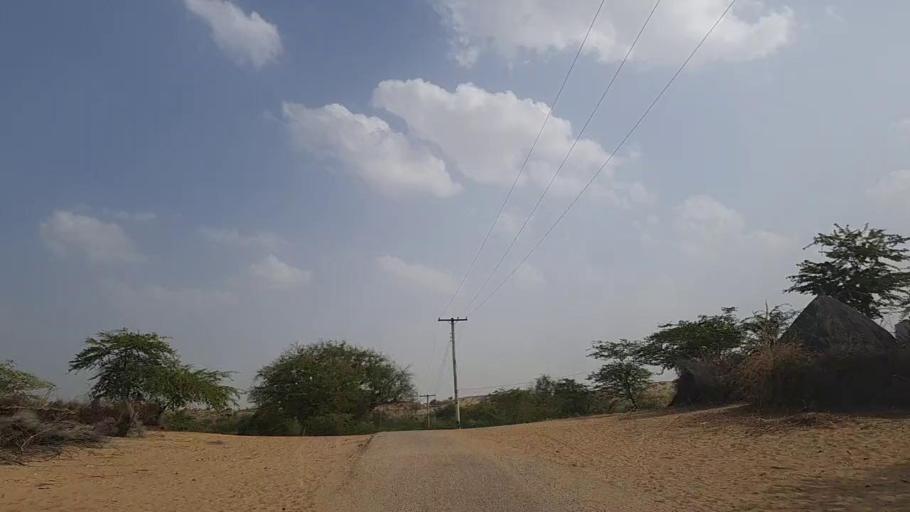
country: PK
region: Sindh
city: Islamkot
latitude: 24.8712
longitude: 70.1660
